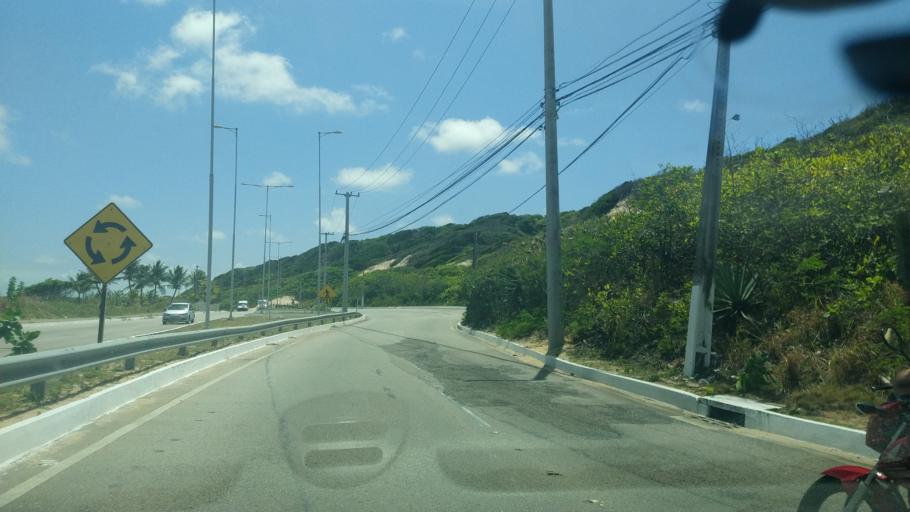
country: BR
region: Rio Grande do Norte
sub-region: Natal
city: Natal
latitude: -5.8019
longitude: -35.1826
